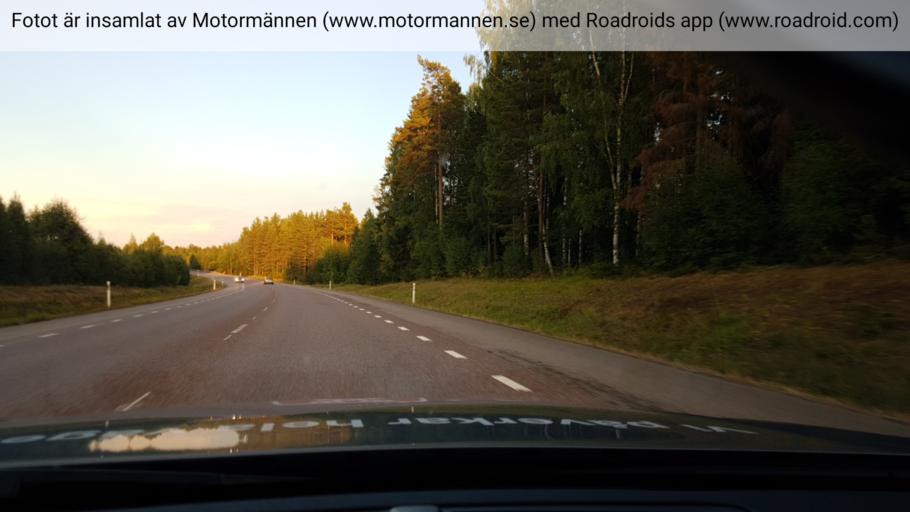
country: SE
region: Dalarna
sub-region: Smedjebackens Kommun
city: Smedjebacken
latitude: 60.0966
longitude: 15.5107
